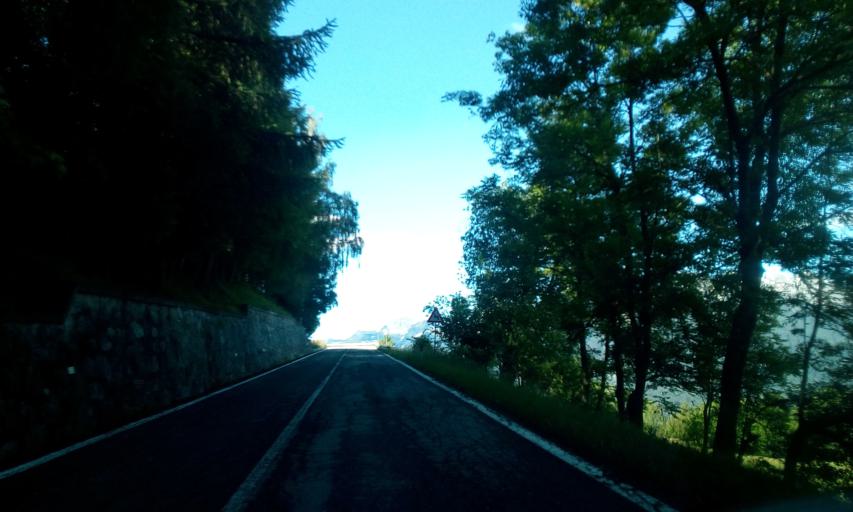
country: IT
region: Aosta Valley
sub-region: Valle d'Aosta
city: Emarese
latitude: 45.7508
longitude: 7.6878
